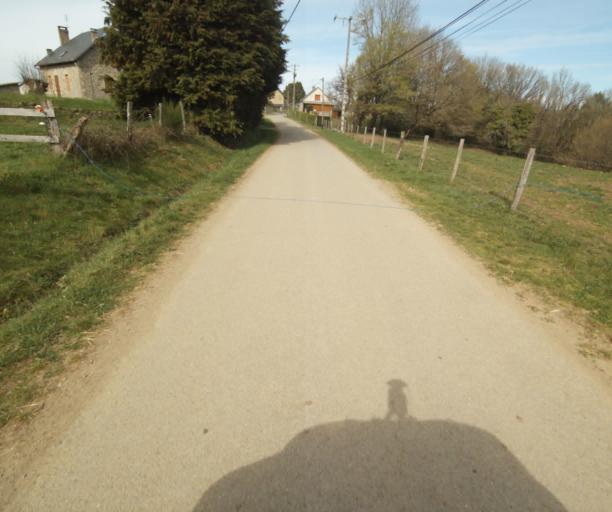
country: FR
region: Limousin
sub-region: Departement de la Correze
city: Correze
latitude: 45.3933
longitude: 1.8103
